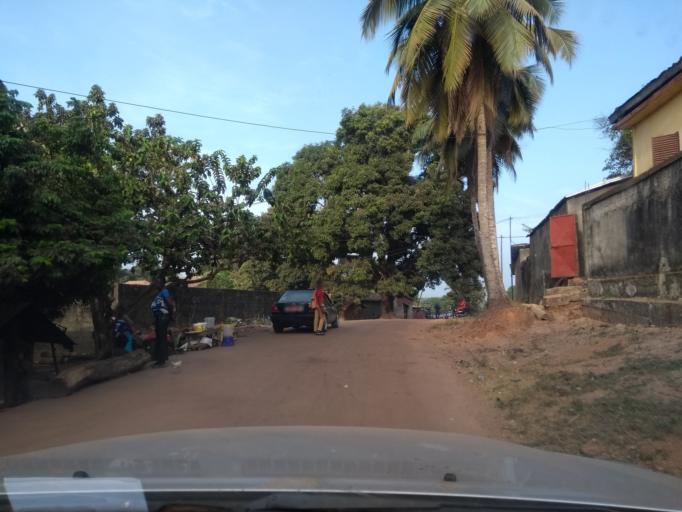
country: GN
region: Kindia
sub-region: Prefecture de Dubreka
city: Dubreka
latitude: 9.7876
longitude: -13.5257
